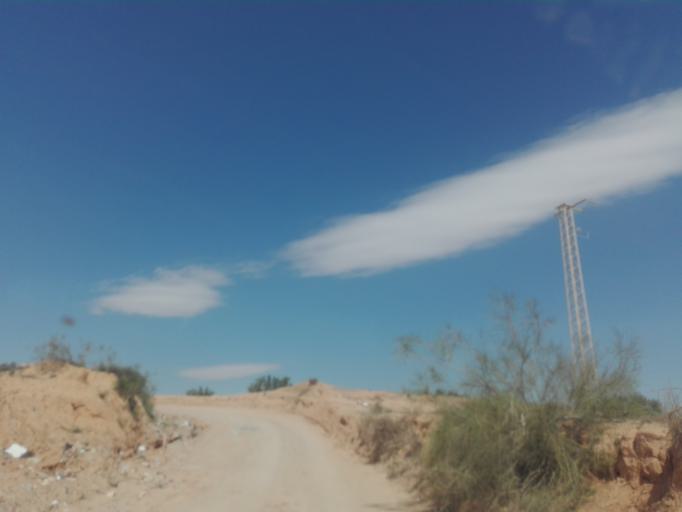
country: TN
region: Safaqis
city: Sfax
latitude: 34.6870
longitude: 10.5593
